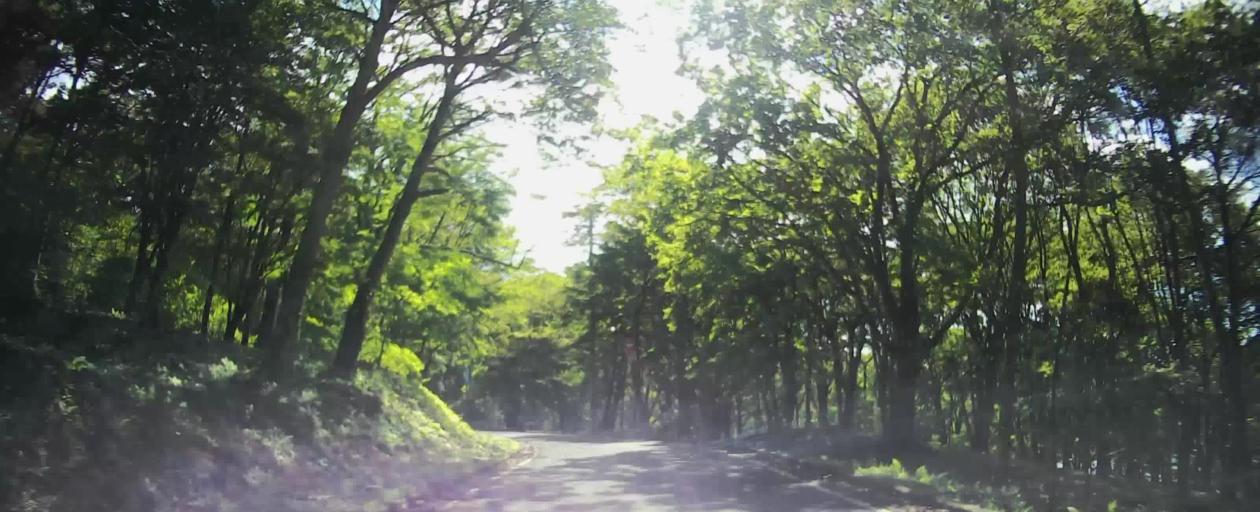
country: JP
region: Gunma
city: Nakanojomachi
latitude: 36.4760
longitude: 138.8715
